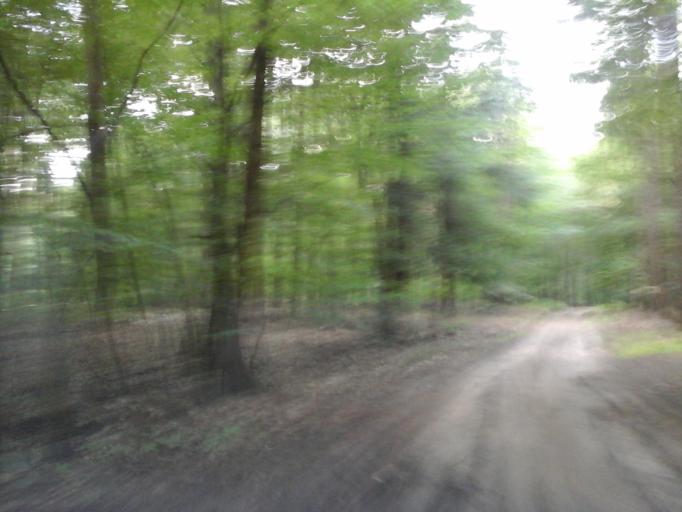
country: PL
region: West Pomeranian Voivodeship
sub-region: Powiat choszczenski
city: Bierzwnik
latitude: 53.0631
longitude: 15.6920
